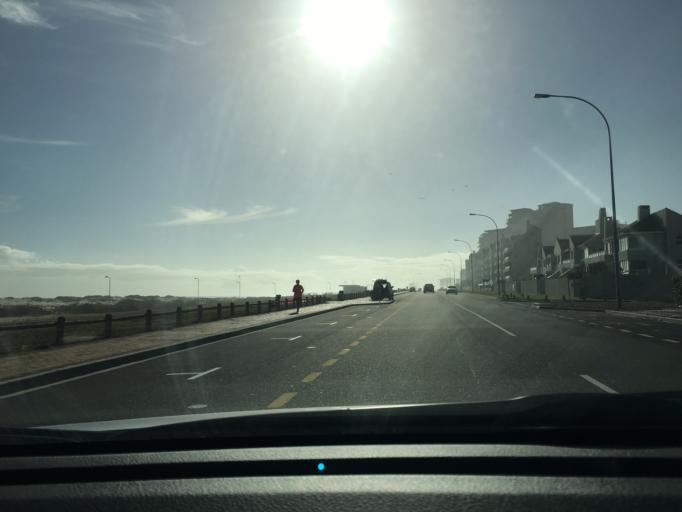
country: ZA
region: Western Cape
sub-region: City of Cape Town
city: Sunset Beach
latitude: -33.8263
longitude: 18.4795
